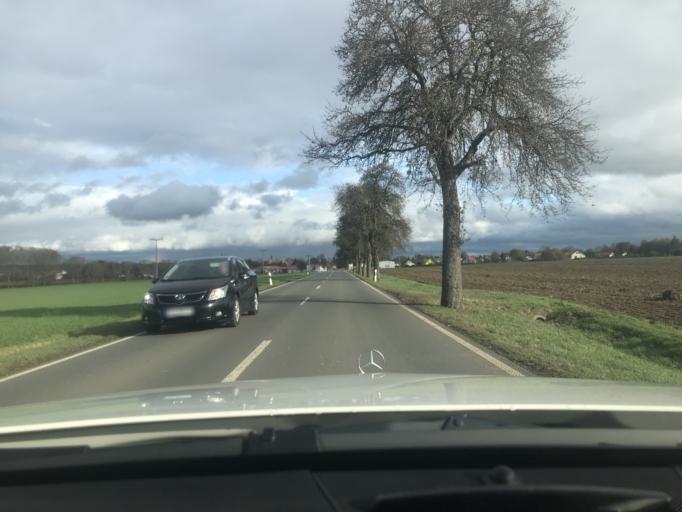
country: DE
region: Thuringia
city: Bufleben
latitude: 50.9992
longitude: 10.7263
